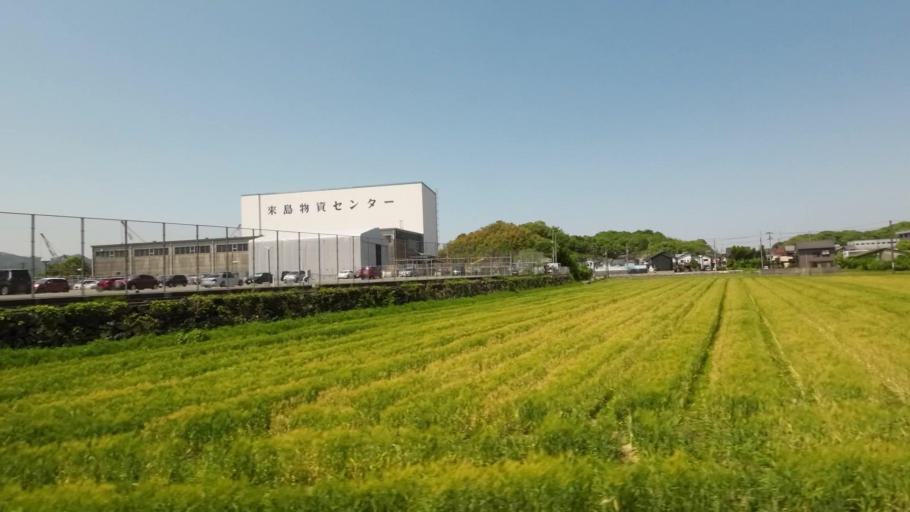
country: JP
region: Ehime
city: Hojo
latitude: 34.0741
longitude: 132.9318
